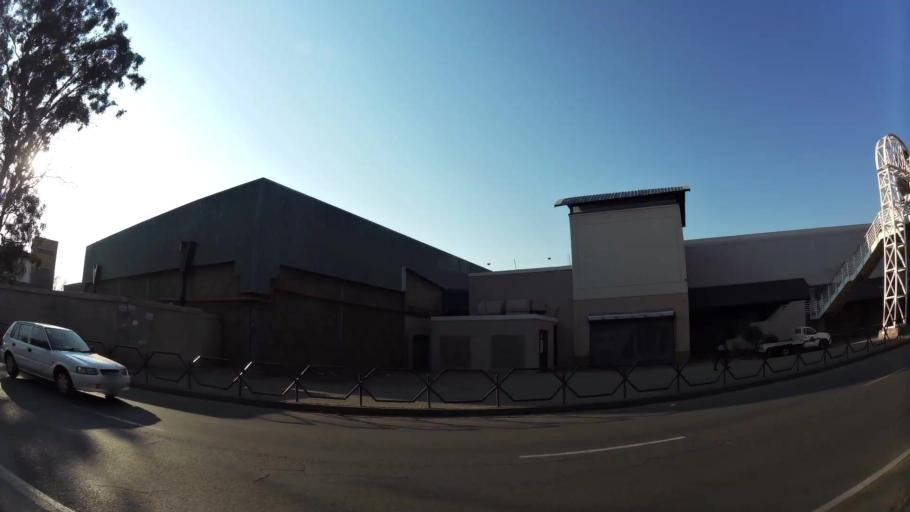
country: ZA
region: Gauteng
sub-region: Ekurhuleni Metropolitan Municipality
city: Germiston
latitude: -26.2128
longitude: 28.1643
